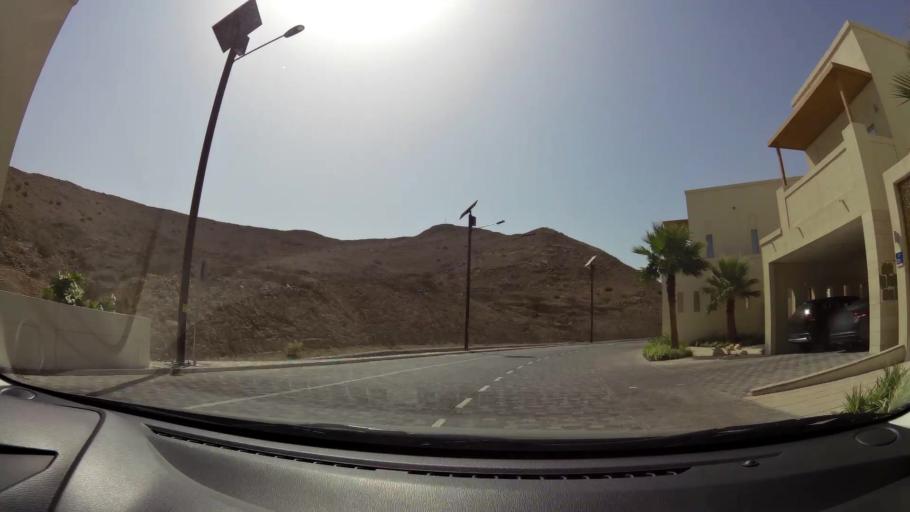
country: OM
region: Muhafazat Masqat
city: Muscat
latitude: 23.6409
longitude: 58.5052
